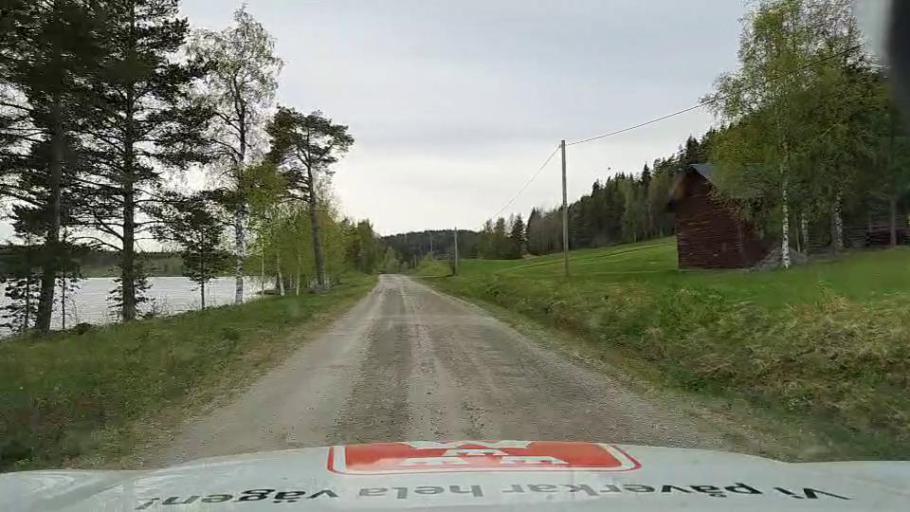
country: SE
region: Jaemtland
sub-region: Bergs Kommun
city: Hoverberg
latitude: 62.6840
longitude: 14.7947
